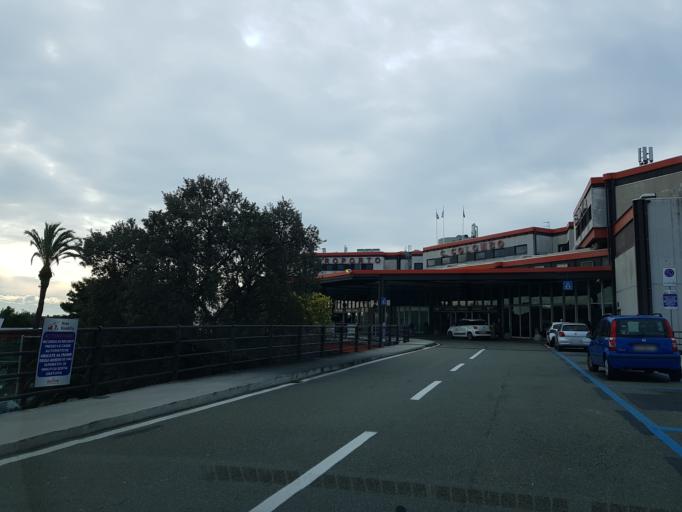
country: IT
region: Liguria
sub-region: Provincia di Genova
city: San Teodoro
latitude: 44.4157
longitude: 8.8508
